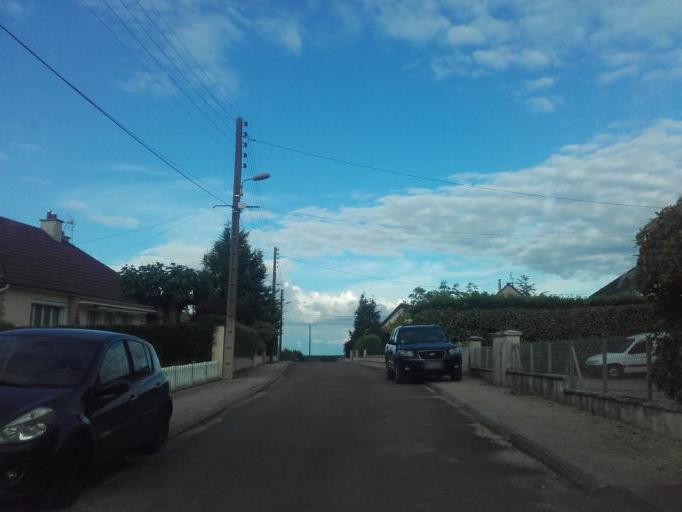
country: FR
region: Bourgogne
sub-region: Departement de Saone-et-Loire
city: Rully
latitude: 46.8716
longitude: 4.7450
